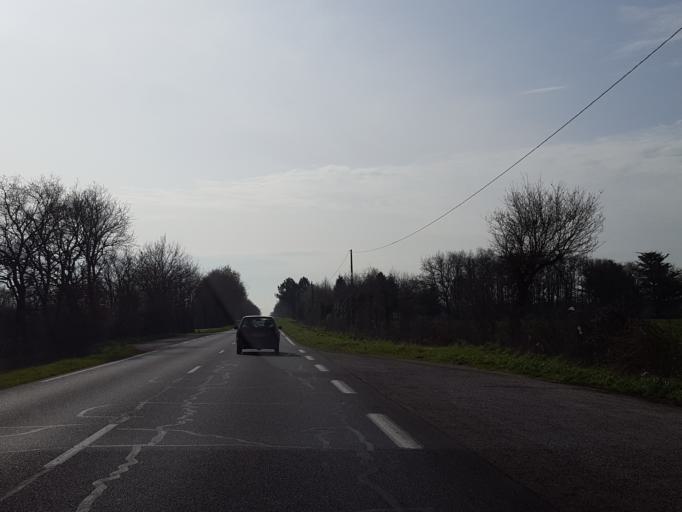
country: FR
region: Pays de la Loire
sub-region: Departement de la Vendee
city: Saligny
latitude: 46.8125
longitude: -1.4616
